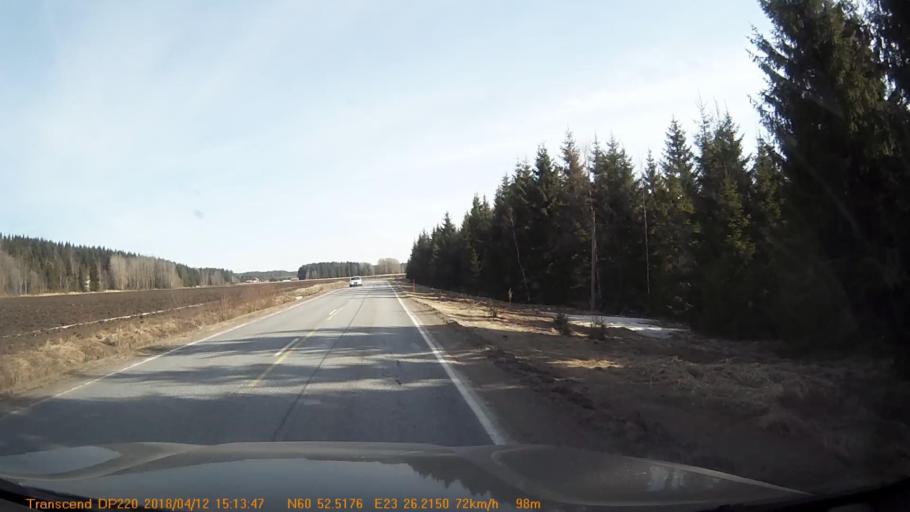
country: FI
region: Haeme
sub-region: Forssa
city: Jokioinen
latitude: 60.8751
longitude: 23.4372
